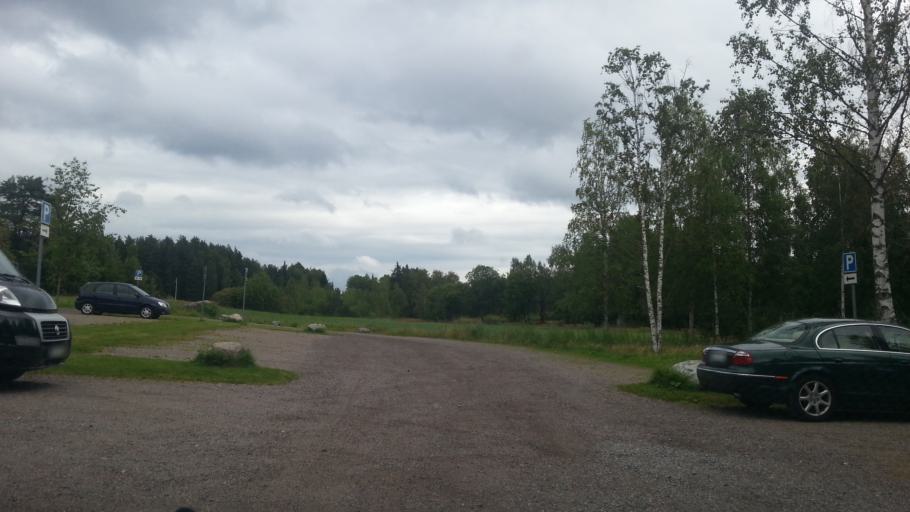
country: SE
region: Dalarna
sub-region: Faluns Kommun
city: Falun
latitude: 60.6535
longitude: 15.7812
